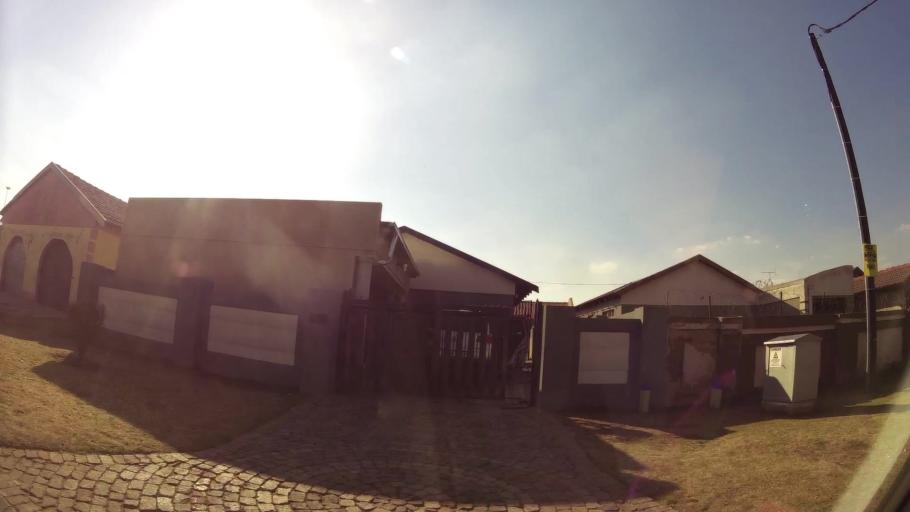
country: ZA
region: Gauteng
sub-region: Ekurhuleni Metropolitan Municipality
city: Benoni
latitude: -26.2229
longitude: 28.3261
